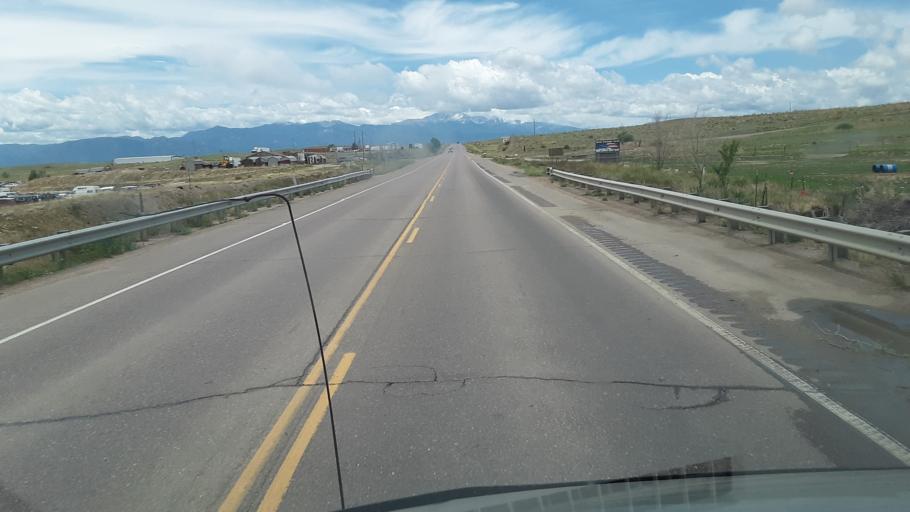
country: US
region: Colorado
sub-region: El Paso County
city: Cimarron Hills
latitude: 38.8386
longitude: -104.5946
